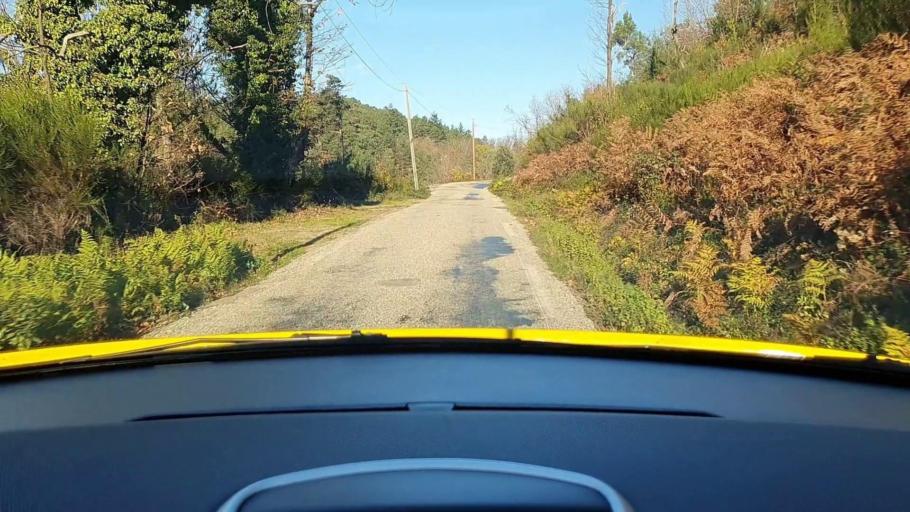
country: FR
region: Languedoc-Roussillon
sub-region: Departement du Gard
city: Branoux-les-Taillades
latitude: 44.2804
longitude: 3.9691
